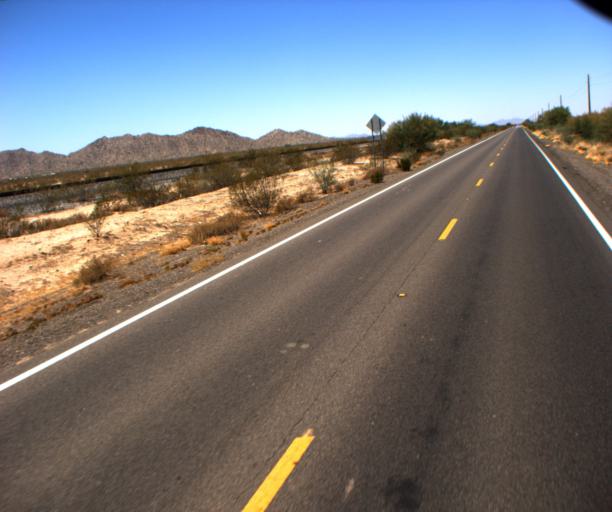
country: US
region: Arizona
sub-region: Pinal County
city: Maricopa
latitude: 33.0766
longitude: -112.1597
